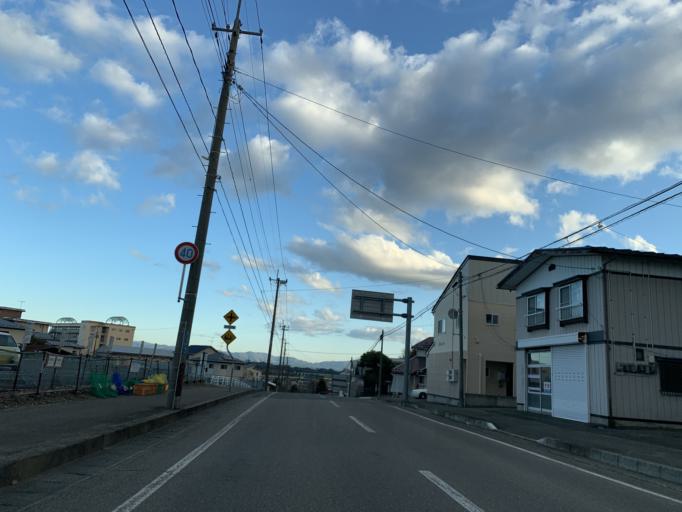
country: JP
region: Iwate
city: Kitakami
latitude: 39.2604
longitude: 141.1034
